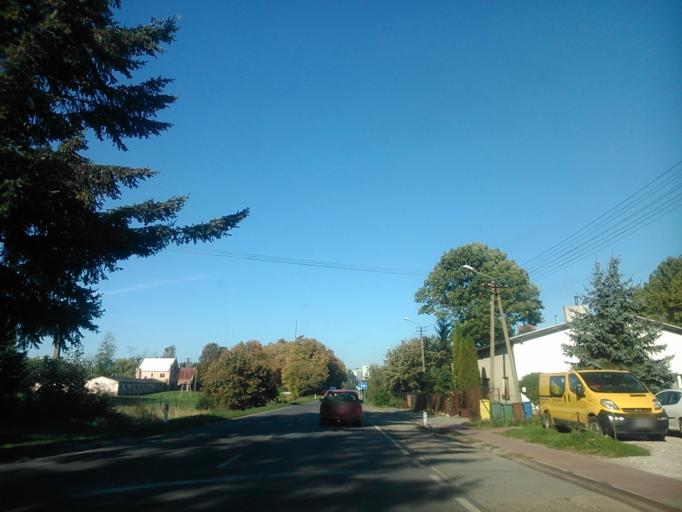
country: PL
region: Kujawsko-Pomorskie
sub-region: Powiat wabrzeski
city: Wabrzezno
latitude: 53.2644
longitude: 18.9954
